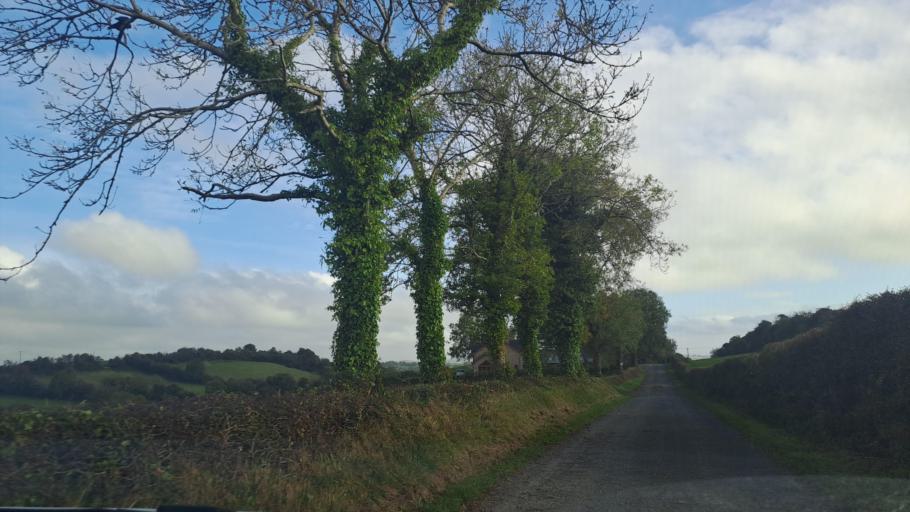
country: IE
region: Ulster
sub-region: County Monaghan
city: Carrickmacross
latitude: 54.0115
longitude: -6.7508
